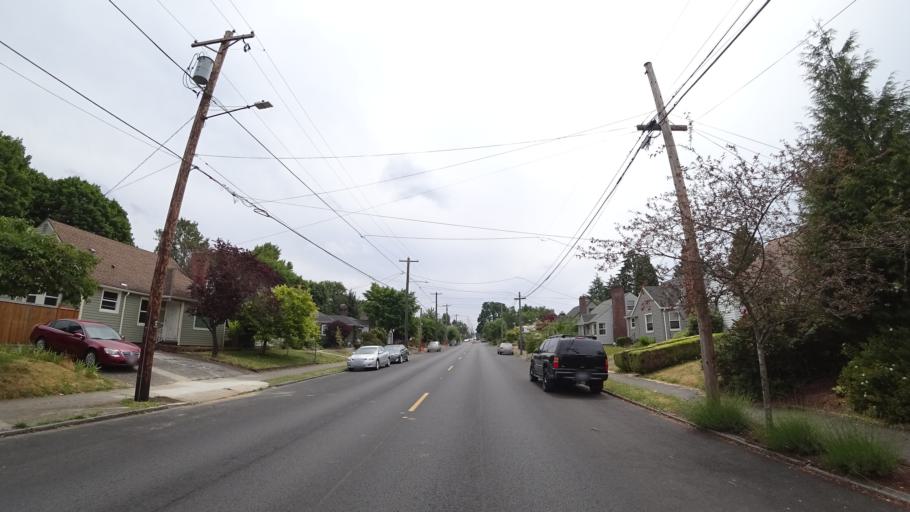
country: US
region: Oregon
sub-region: Multnomah County
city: Portland
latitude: 45.5733
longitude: -122.6955
